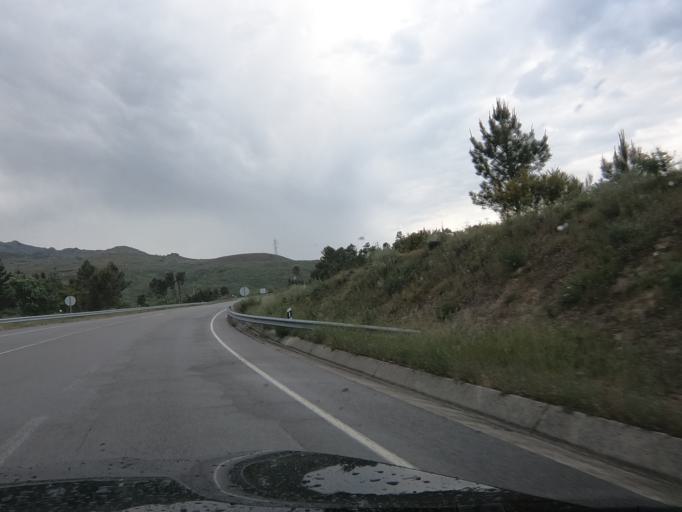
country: PT
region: Vila Real
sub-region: Vila Real
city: Vila Real
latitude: 41.3740
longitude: -7.7143
